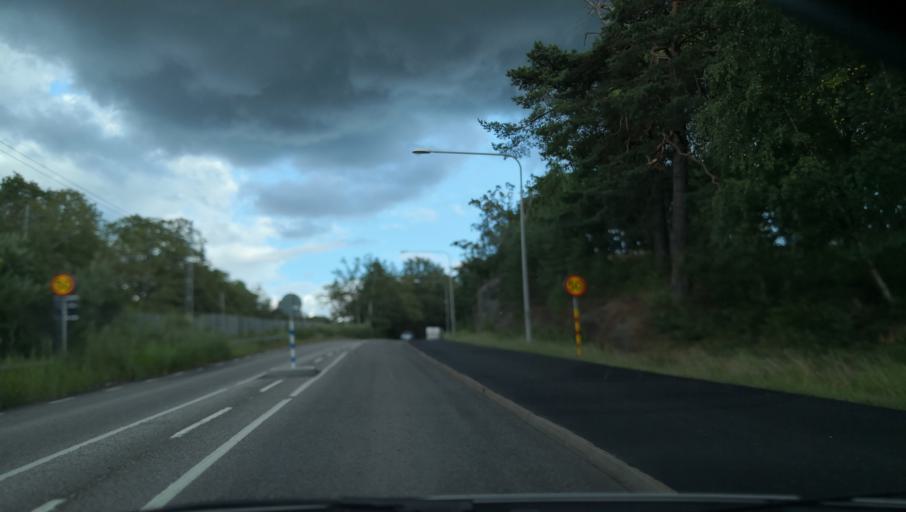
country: SE
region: Stockholm
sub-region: Stockholms Kommun
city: Arsta
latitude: 59.2396
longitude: 18.0886
